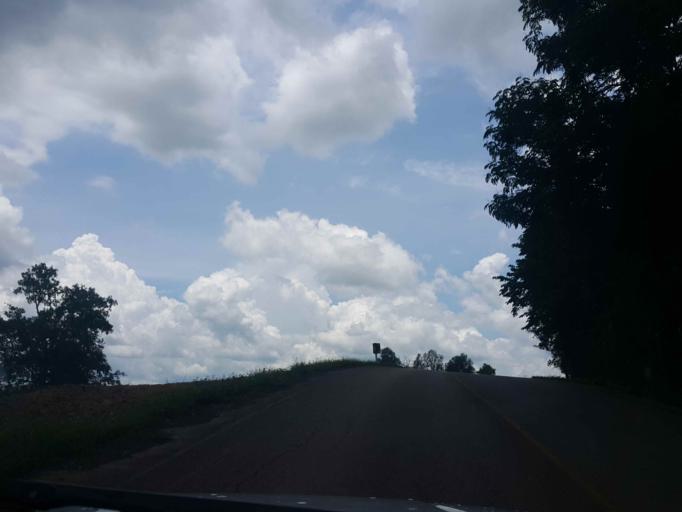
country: TH
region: Lampang
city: Ngao
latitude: 18.9458
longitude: 100.0781
